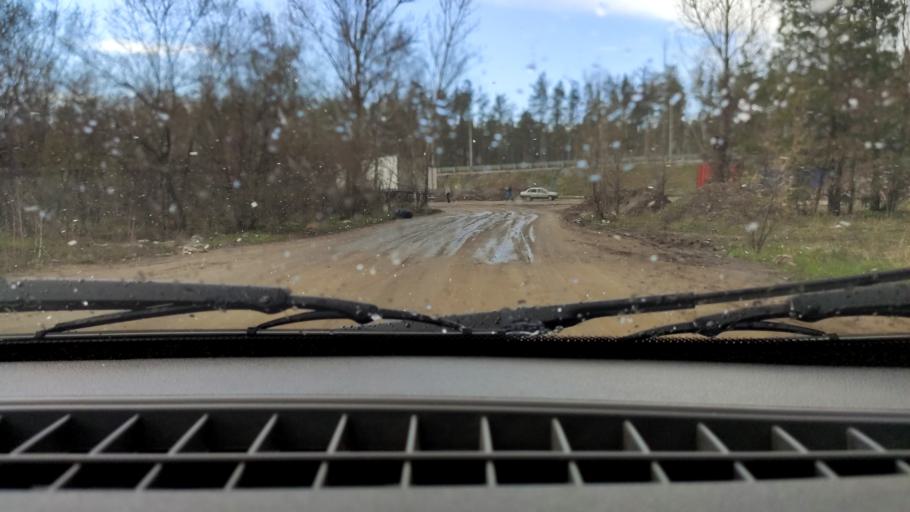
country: RU
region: Voronezj
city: Somovo
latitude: 51.7408
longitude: 39.3037
